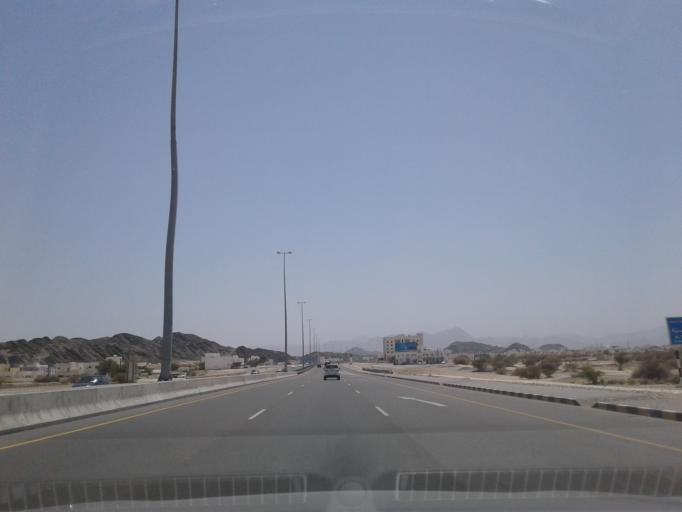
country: OM
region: Muhafazat Masqat
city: Bawshar
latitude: 23.4895
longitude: 58.5001
